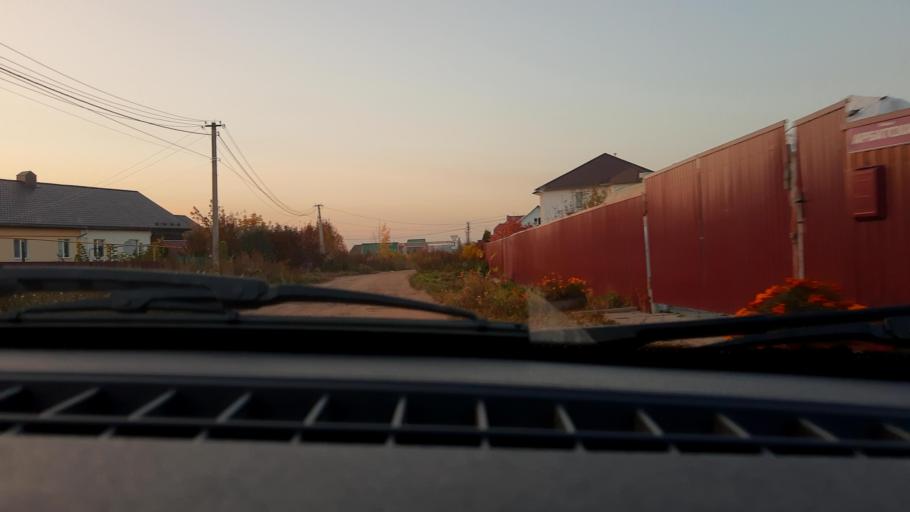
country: RU
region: Bashkortostan
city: Mikhaylovka
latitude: 54.7812
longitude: 55.9040
